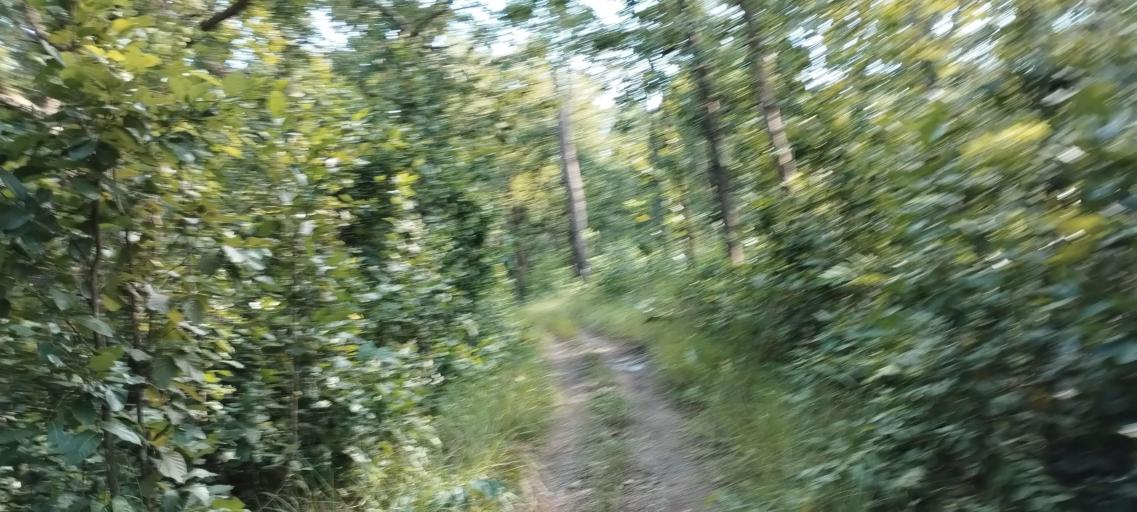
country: NP
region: Far Western
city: Tikapur
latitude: 28.5464
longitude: 81.2865
